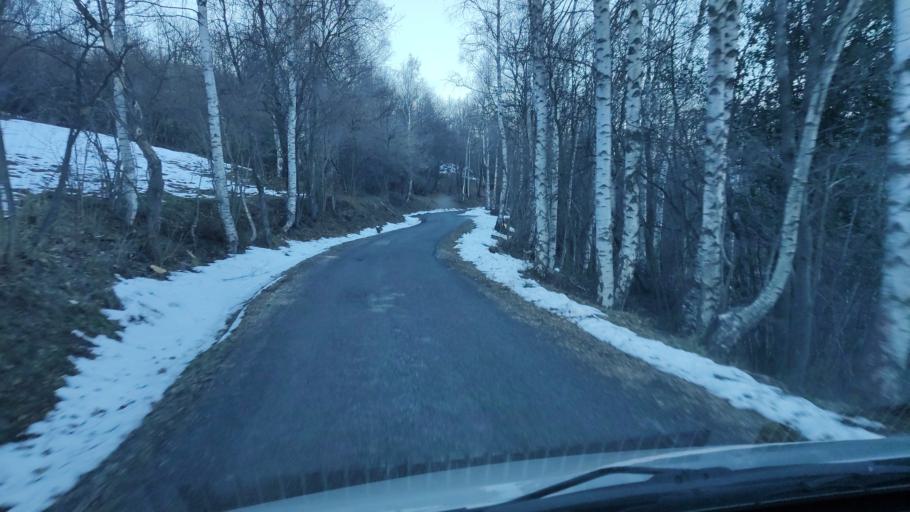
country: IT
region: Piedmont
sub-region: Provincia di Cuneo
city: Viola
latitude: 44.2732
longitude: 7.9925
